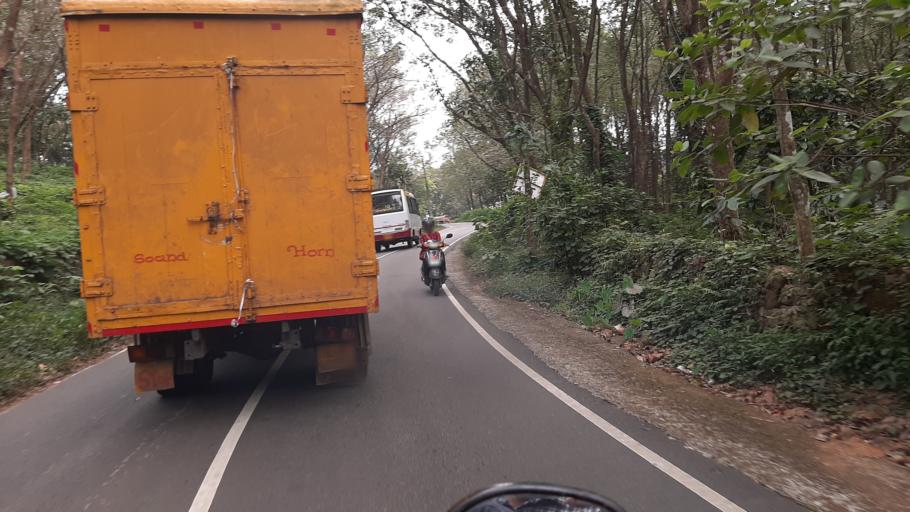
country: IN
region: Kerala
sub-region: Pattanamtitta
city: Pathanamthitta
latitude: 9.4656
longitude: 76.8704
